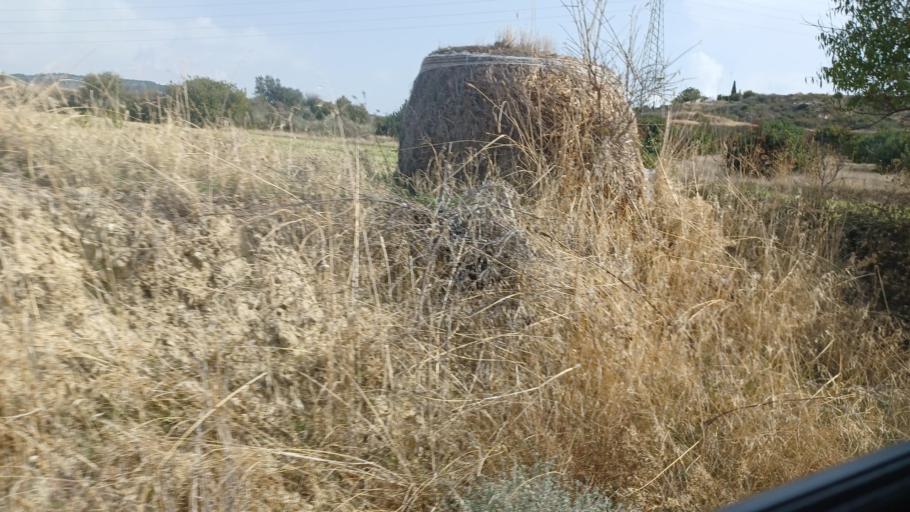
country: CY
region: Pafos
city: Polis
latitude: 34.9913
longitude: 32.4539
